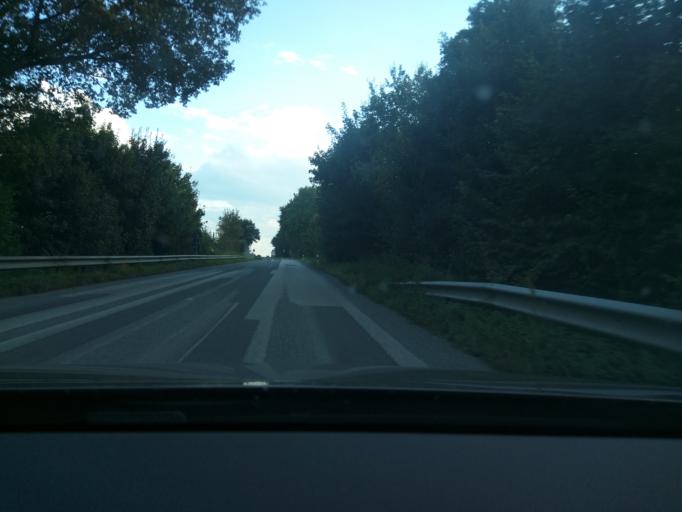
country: DE
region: Schleswig-Holstein
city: Kruzen
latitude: 53.4173
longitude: 10.5366
